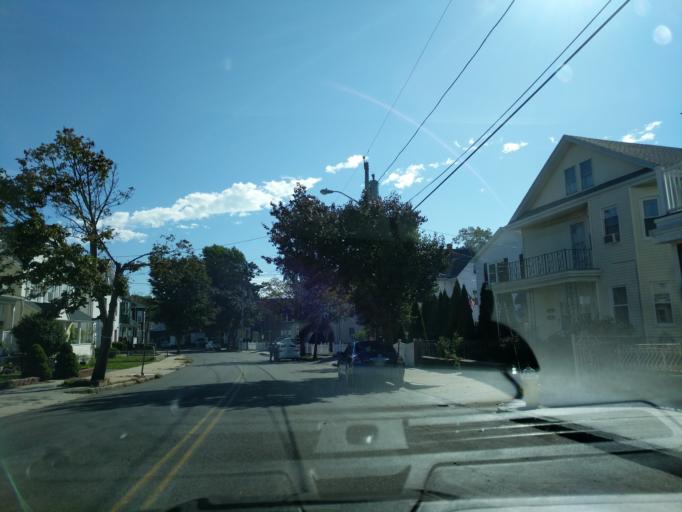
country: US
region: Massachusetts
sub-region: Suffolk County
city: Revere
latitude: 42.4062
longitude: -71.0136
